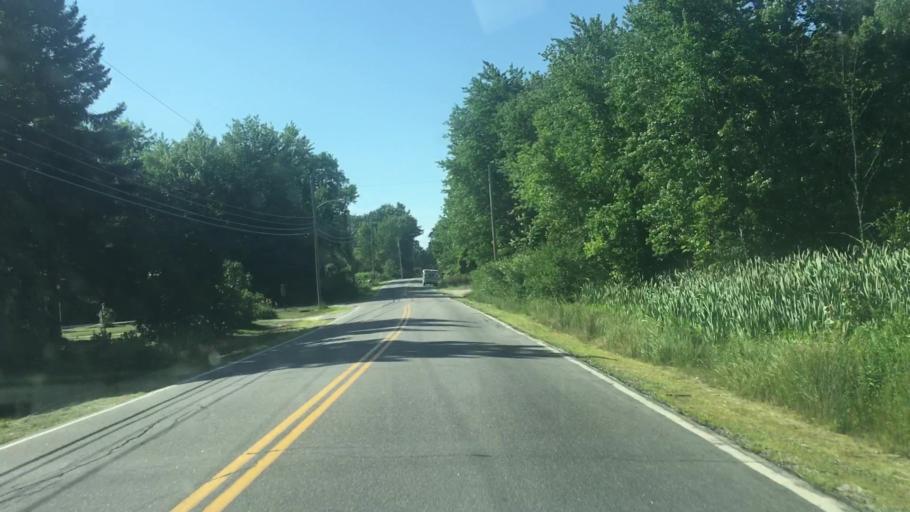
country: US
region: Maine
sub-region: York County
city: Buxton
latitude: 43.6213
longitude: -70.5450
